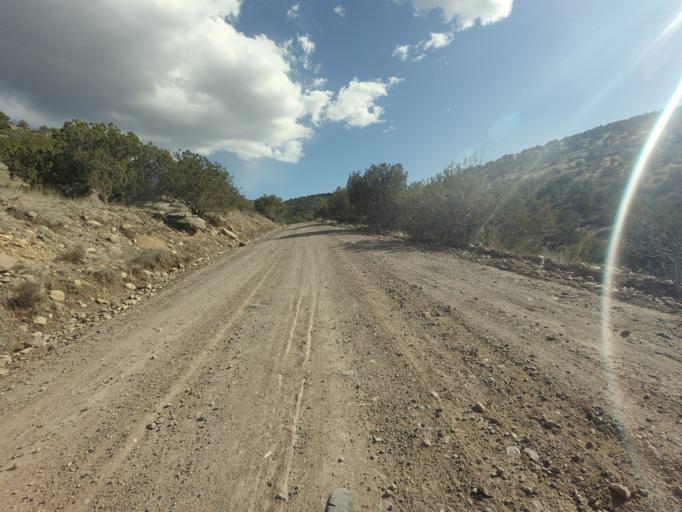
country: US
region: Arizona
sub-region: Yavapai County
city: Camp Verde
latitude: 34.4296
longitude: -111.6879
